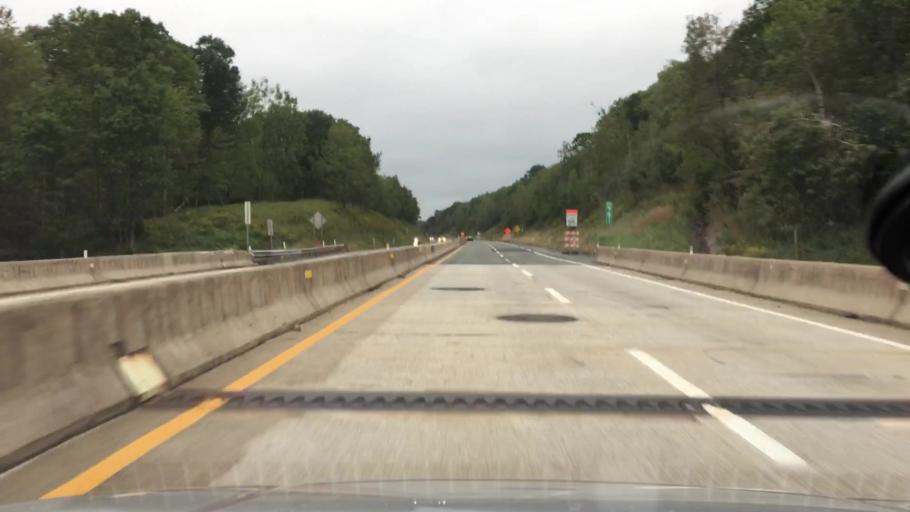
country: US
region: Pennsylvania
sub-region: Luzerne County
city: White Haven
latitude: 41.1047
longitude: -75.7500
